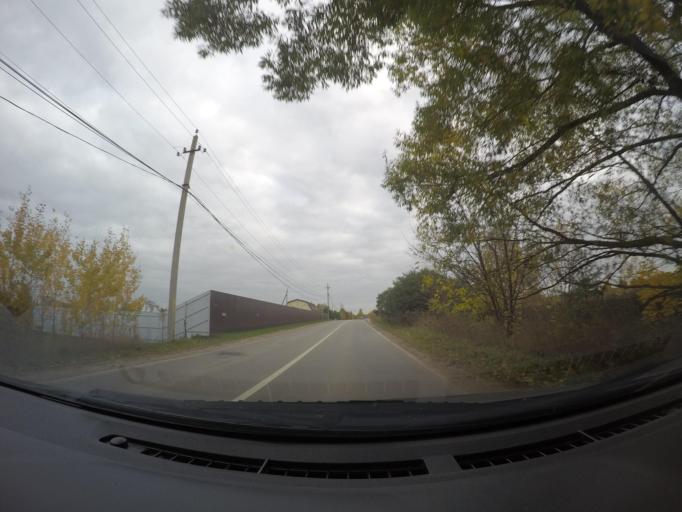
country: RU
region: Moskovskaya
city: Gzhel'
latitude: 55.6411
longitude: 38.3952
